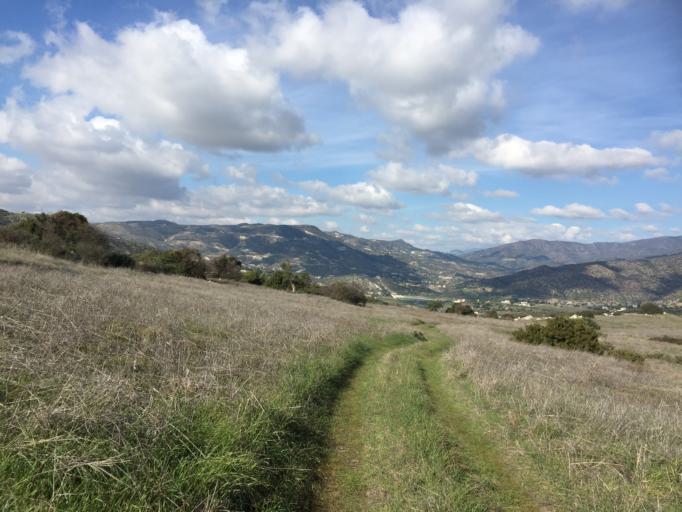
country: CY
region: Larnaka
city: Agios Tychon
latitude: 34.7464
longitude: 33.1175
